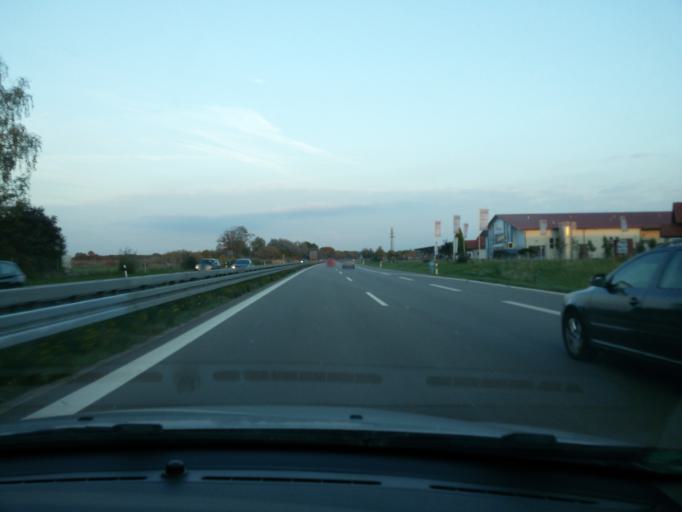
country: DE
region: Bavaria
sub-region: Swabia
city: Turkheim
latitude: 48.0410
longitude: 10.6243
